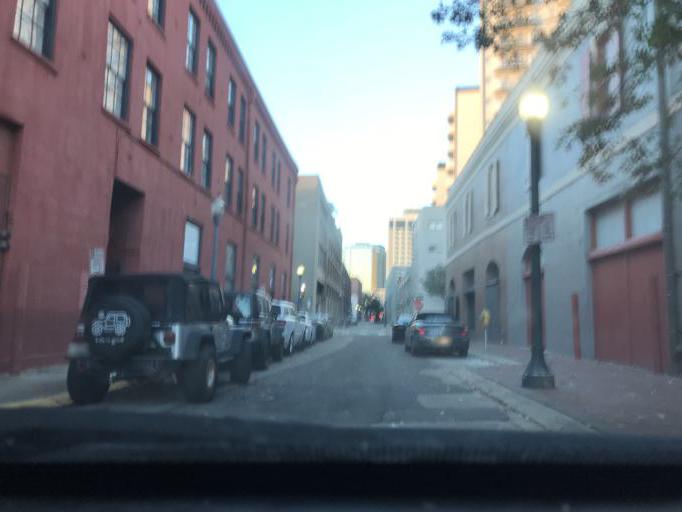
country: US
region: Louisiana
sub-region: Orleans Parish
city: New Orleans
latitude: 29.9443
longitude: -90.0667
